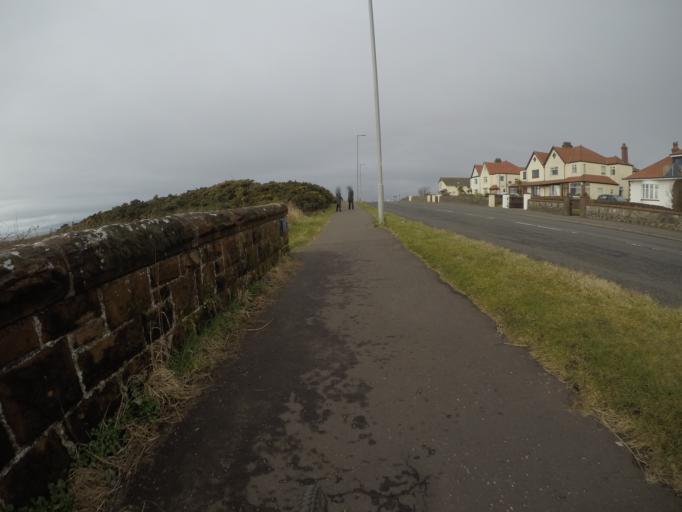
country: GB
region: Scotland
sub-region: North Ayrshire
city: Ardrossan
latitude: 55.6525
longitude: -4.8216
